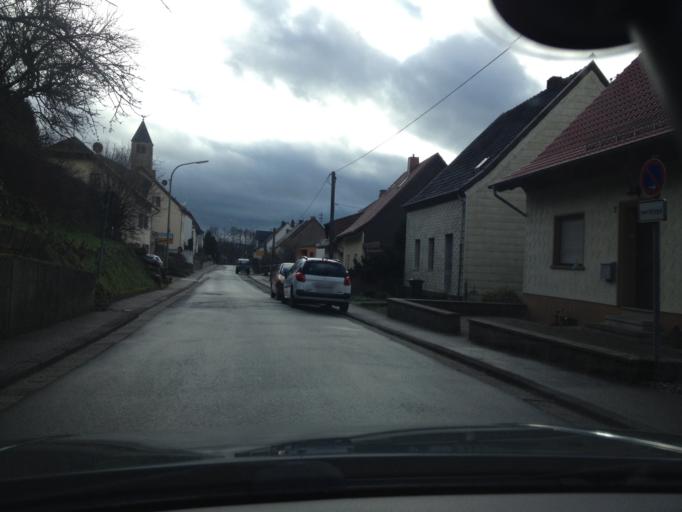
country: DE
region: Saarland
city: Namborn
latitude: 49.4996
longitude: 7.1591
